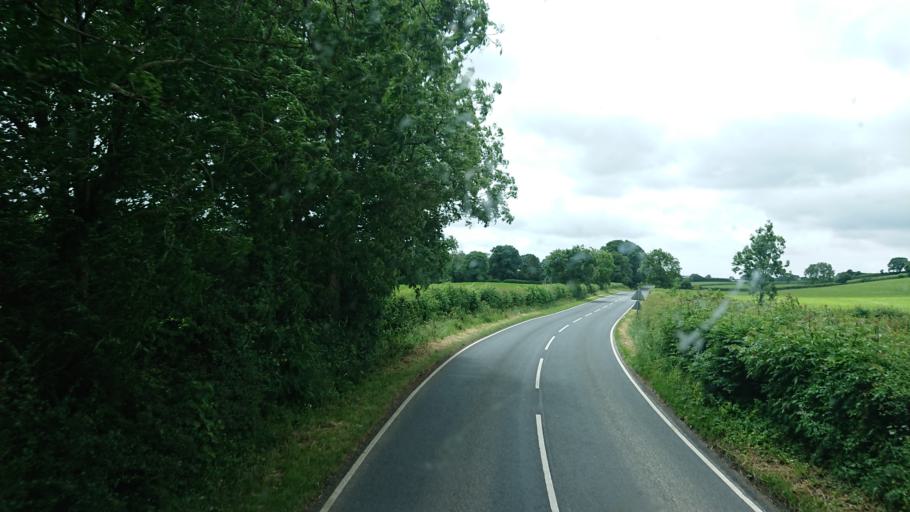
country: GB
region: England
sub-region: Cumbria
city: Milnthorpe
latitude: 54.2392
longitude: -2.7387
